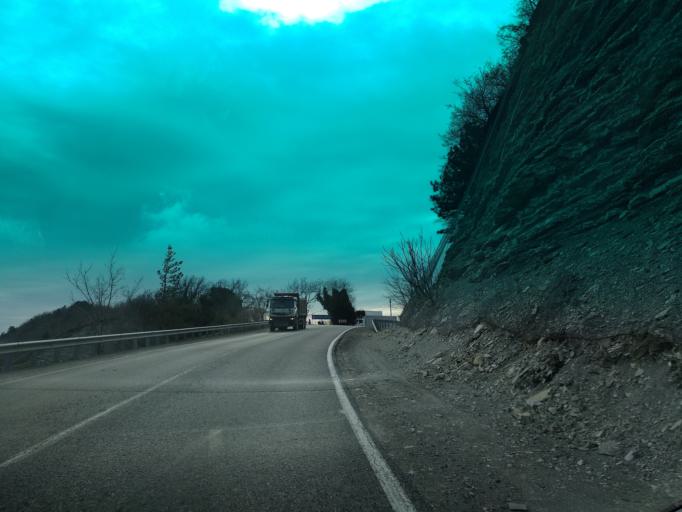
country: RU
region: Krasnodarskiy
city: Tuapse
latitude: 44.0877
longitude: 39.1254
